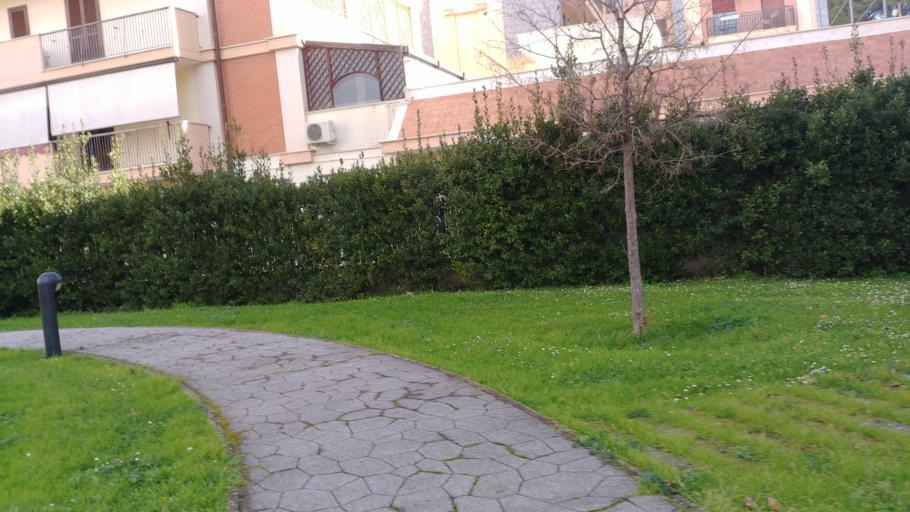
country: IT
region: Apulia
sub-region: Provincia di Barletta - Andria - Trani
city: Andria
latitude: 41.2351
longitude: 16.3056
